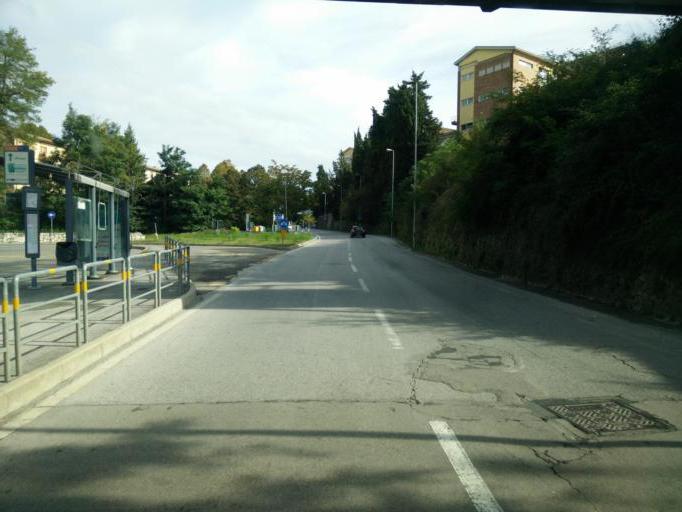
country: IT
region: Tuscany
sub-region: Provincia di Siena
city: Siena
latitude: 43.3237
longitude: 11.3198
